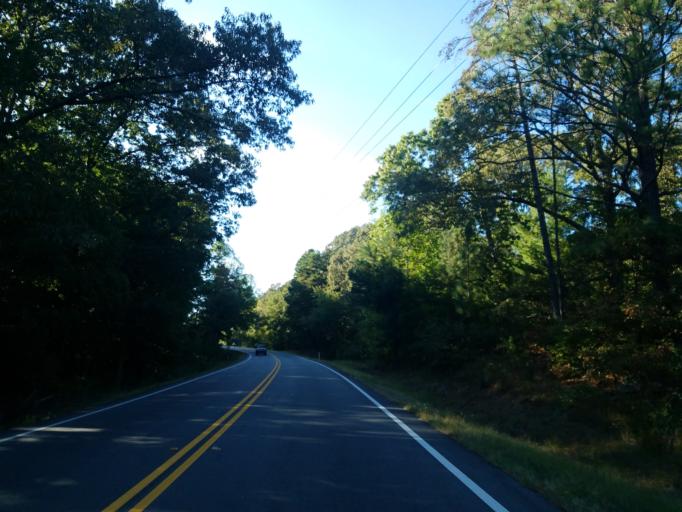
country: US
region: Georgia
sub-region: Bartow County
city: Emerson
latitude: 34.0794
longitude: -84.8329
